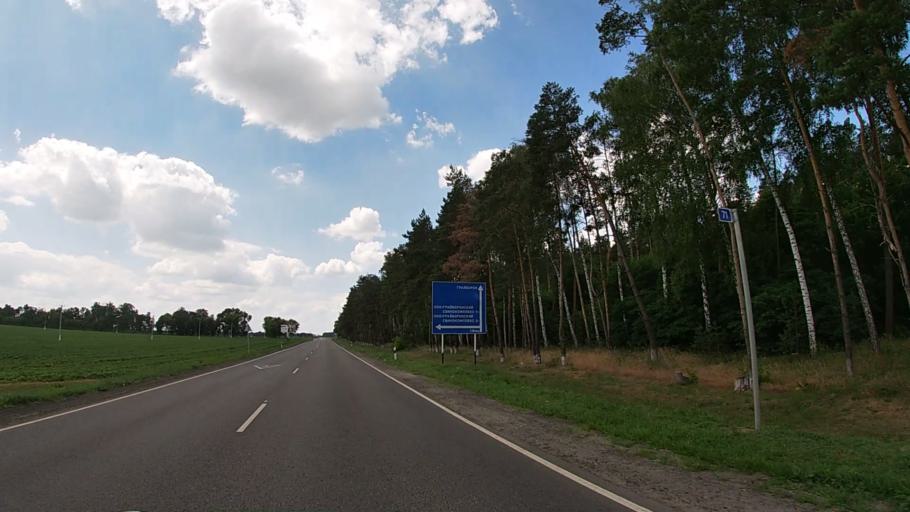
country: RU
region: Belgorod
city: Golovchino
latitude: 50.5074
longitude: 35.7456
